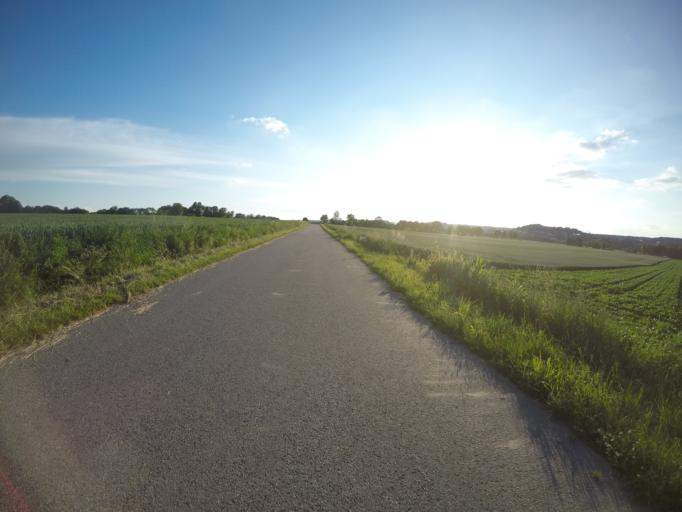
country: DE
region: Bavaria
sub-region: Lower Bavaria
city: Reisbach
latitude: 48.5662
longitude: 12.6030
